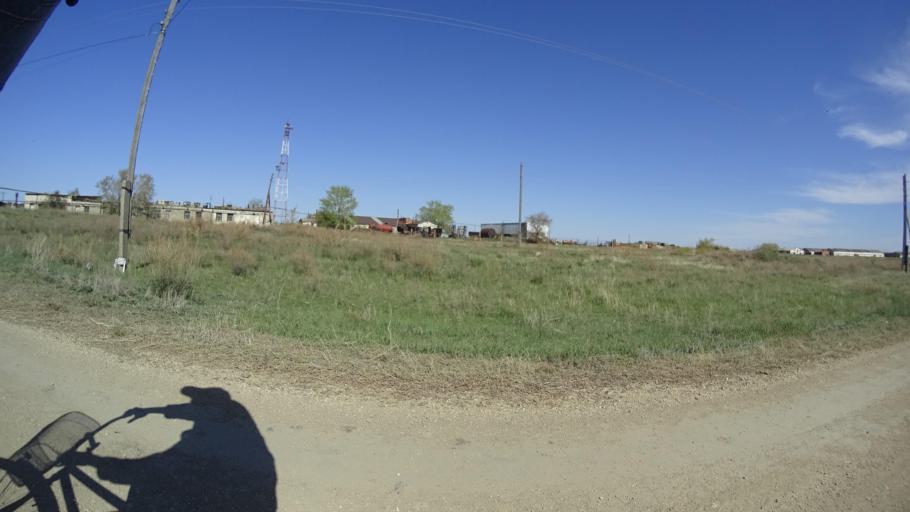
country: RU
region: Chelyabinsk
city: Chesma
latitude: 53.7878
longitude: 61.0395
